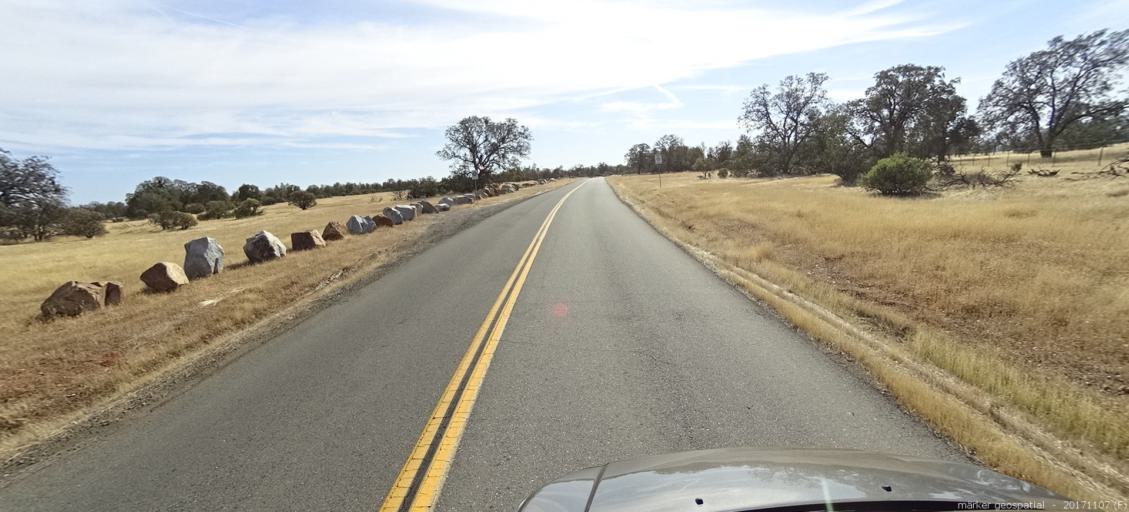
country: US
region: California
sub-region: Shasta County
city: Shasta
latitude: 40.4882
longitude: -122.5485
